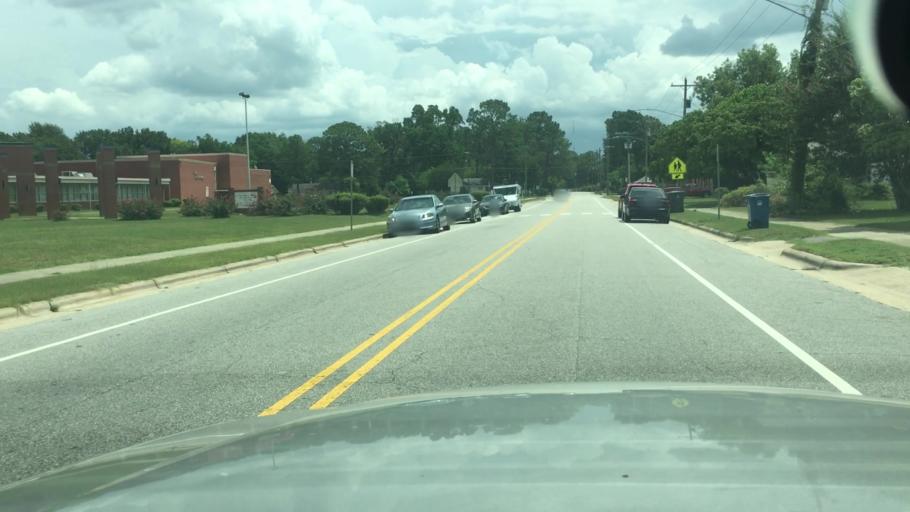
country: US
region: North Carolina
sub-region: Cumberland County
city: Fayetteville
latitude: 35.0844
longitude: -78.8973
